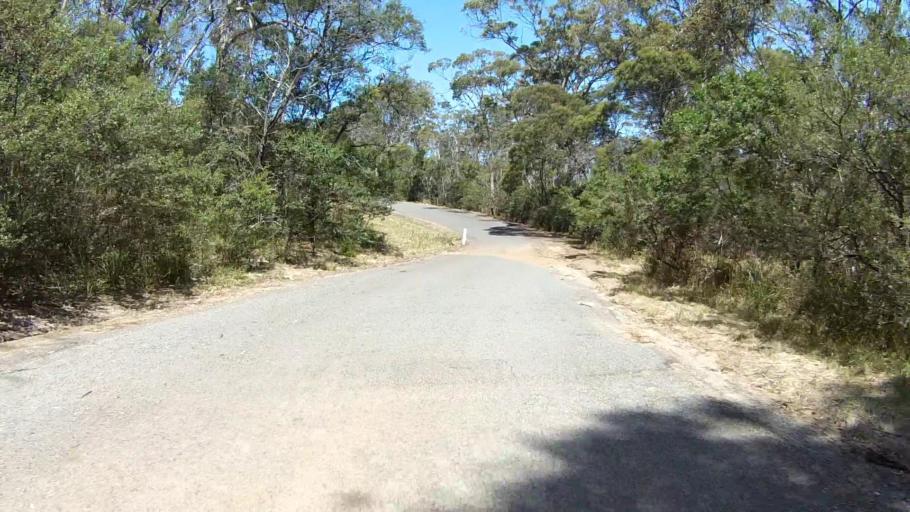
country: AU
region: Tasmania
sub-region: Clarence
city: Sandford
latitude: -43.0189
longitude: 147.4760
